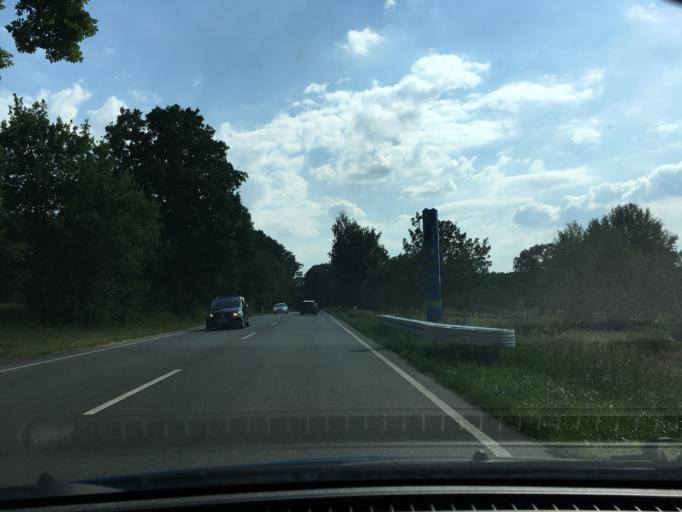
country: DE
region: Lower Saxony
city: Welle
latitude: 53.2473
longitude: 9.8074
